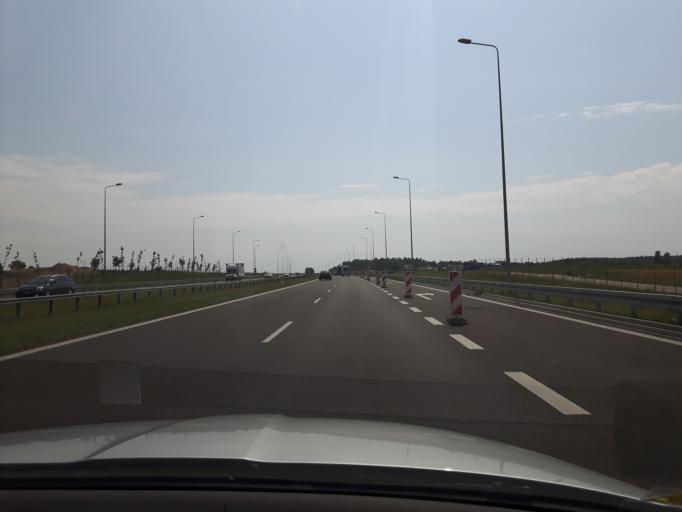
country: PL
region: Warmian-Masurian Voivodeship
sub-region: Powiat nidzicki
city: Nidzica
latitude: 53.3031
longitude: 20.4363
